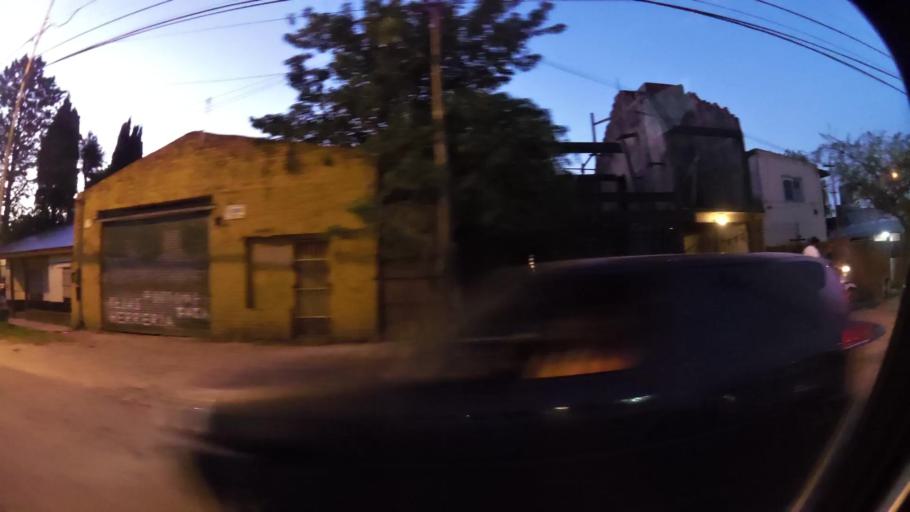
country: AR
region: Buenos Aires
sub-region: Partido de Quilmes
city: Quilmes
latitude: -34.7843
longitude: -58.1847
